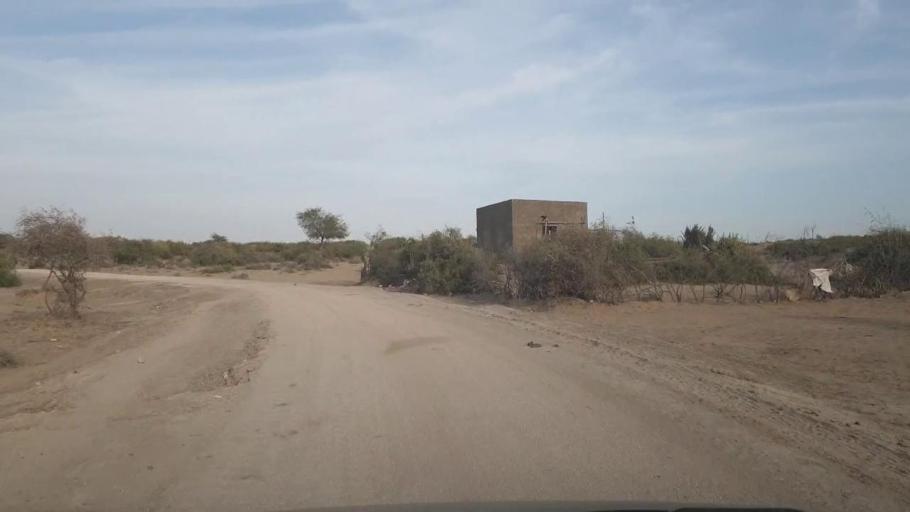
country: PK
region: Sindh
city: Nabisar
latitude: 25.0638
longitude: 69.6458
